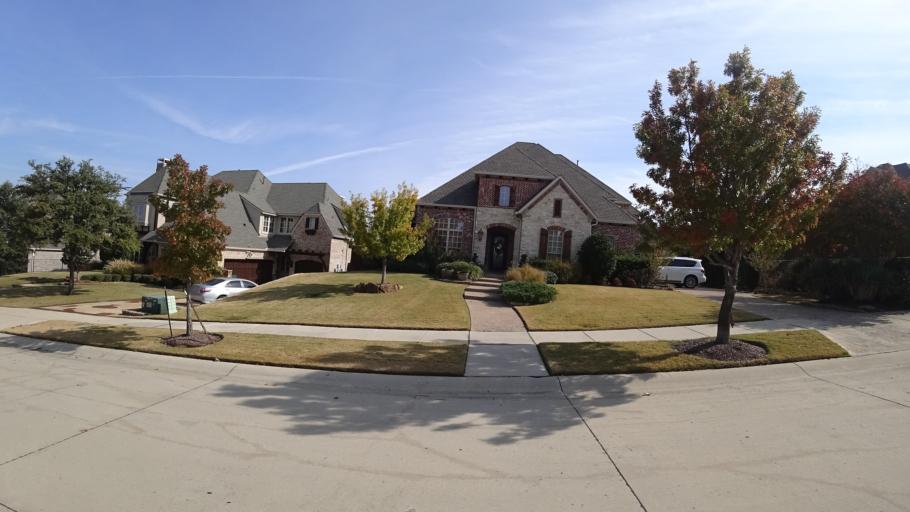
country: US
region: Texas
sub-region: Denton County
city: The Colony
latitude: 33.0374
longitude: -96.8884
